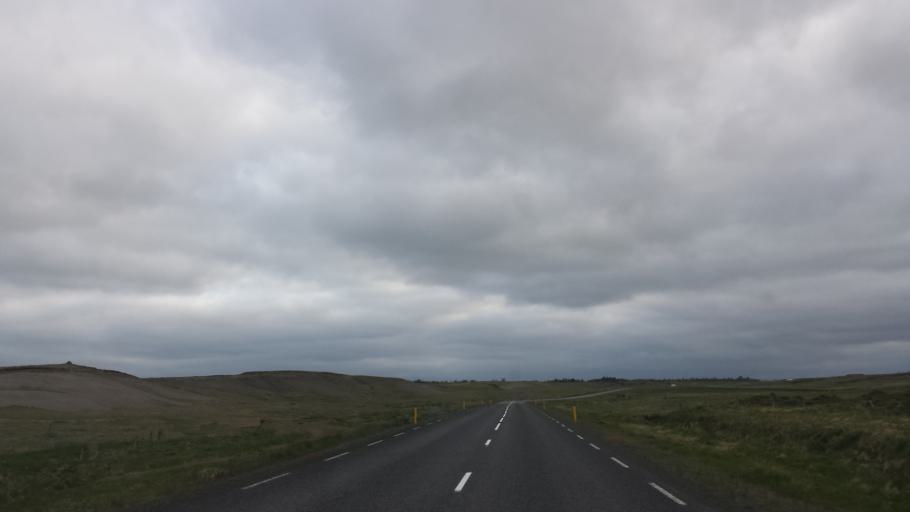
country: IS
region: South
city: Selfoss
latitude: 64.1265
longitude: -20.5917
